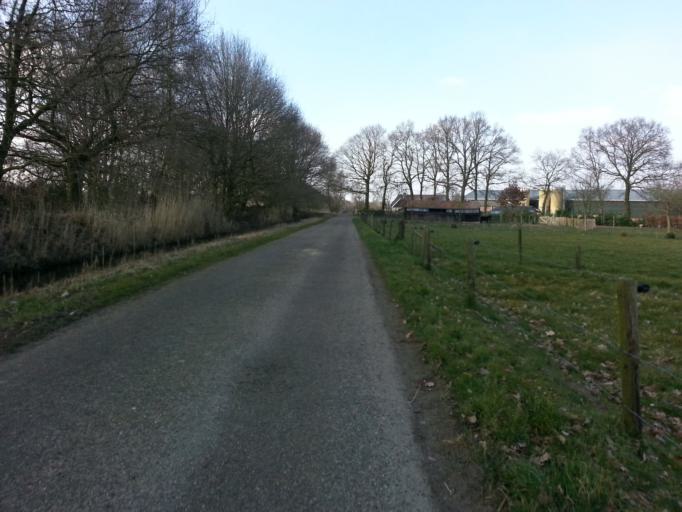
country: NL
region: Utrecht
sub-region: Gemeente Woudenberg
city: Woudenberg
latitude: 52.0901
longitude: 5.4417
